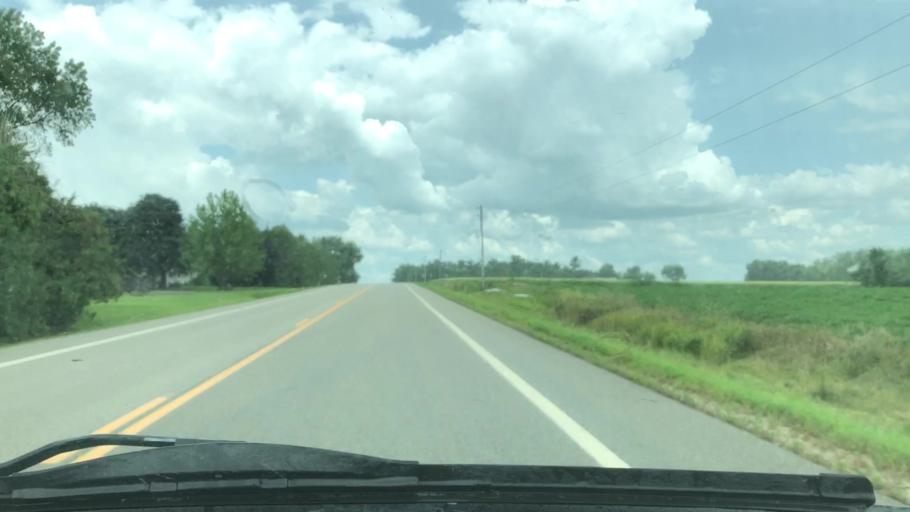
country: US
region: Minnesota
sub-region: Olmsted County
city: Stewartville
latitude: 43.8797
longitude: -92.5285
